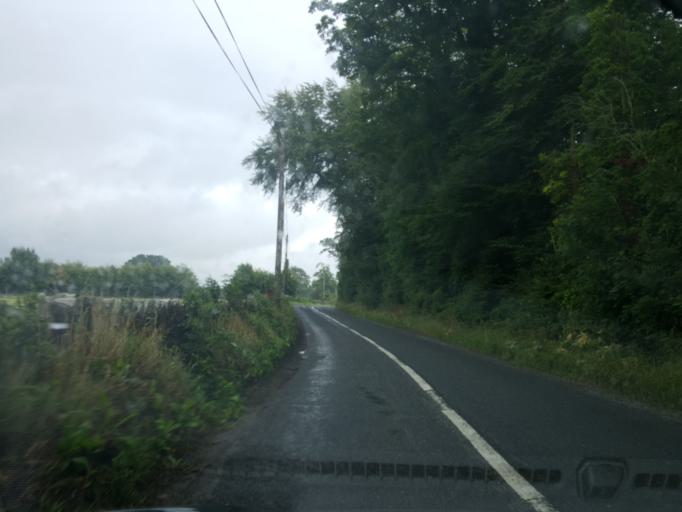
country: IE
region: Leinster
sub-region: Kildare
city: Kilcullen
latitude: 53.1204
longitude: -6.6701
